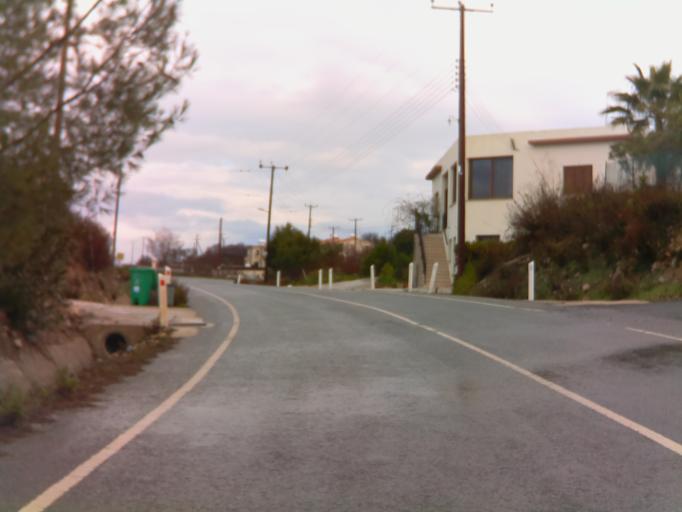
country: CY
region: Pafos
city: Pegeia
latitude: 34.9126
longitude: 32.4215
